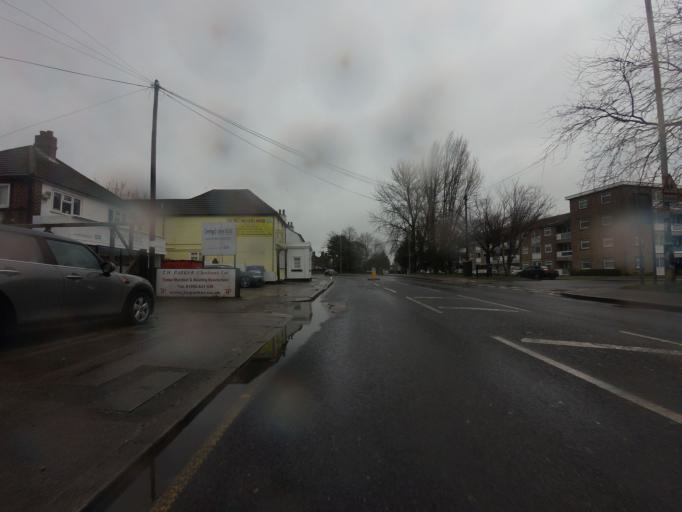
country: GB
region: England
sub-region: Hertfordshire
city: Cheshunt
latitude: 51.7046
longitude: -0.0342
